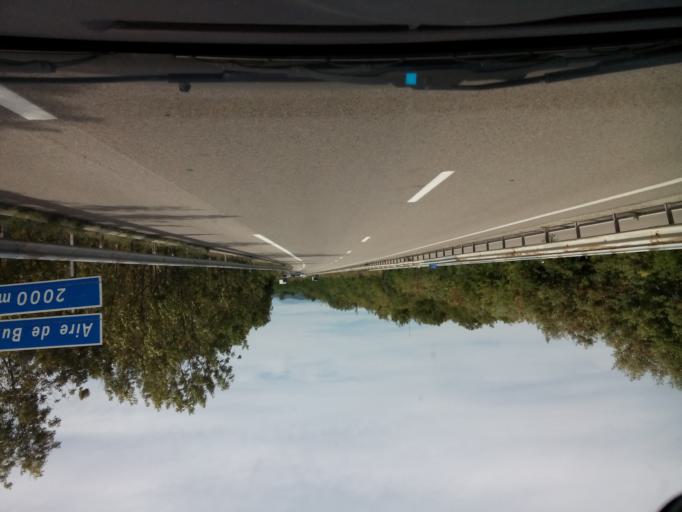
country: FR
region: Rhone-Alpes
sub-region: Departement de l'Isere
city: Chabons
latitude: 45.4377
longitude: 5.4156
